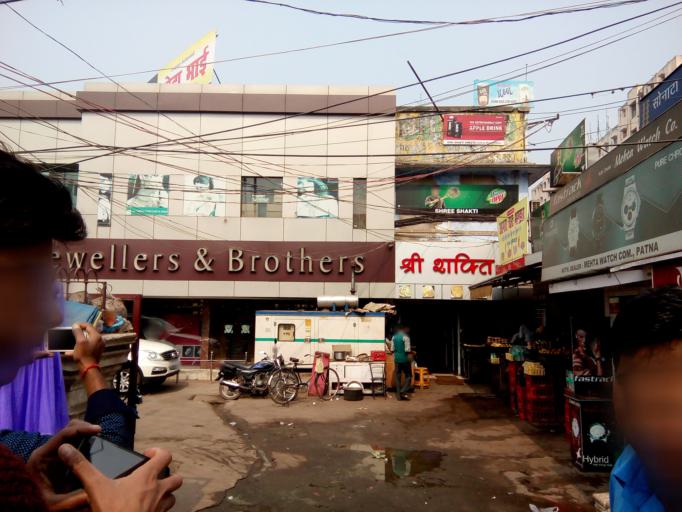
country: IN
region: Bihar
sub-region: Patna
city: Patna
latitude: 25.6149
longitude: 85.1527
